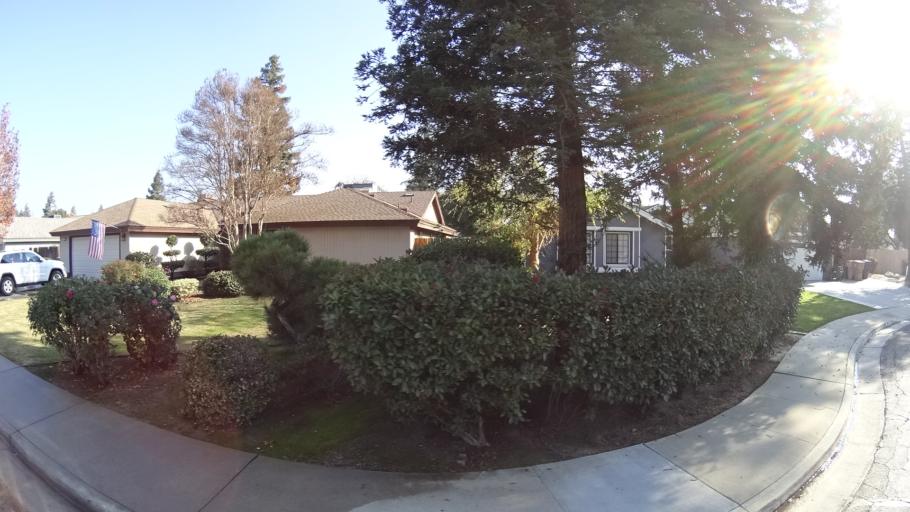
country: US
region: California
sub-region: Kern County
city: Greenacres
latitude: 35.3311
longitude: -119.1084
